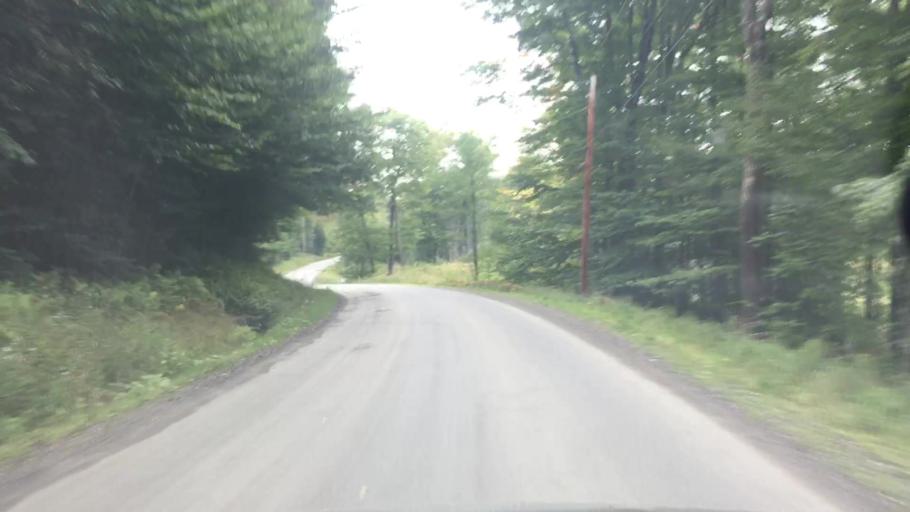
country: US
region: Vermont
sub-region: Windham County
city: Dover
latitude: 42.8372
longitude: -72.8146
